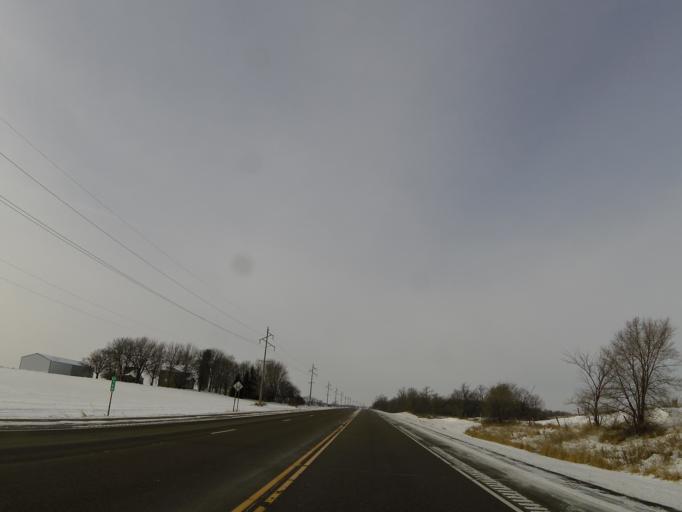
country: US
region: Minnesota
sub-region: Carver County
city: Mayer
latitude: 44.9056
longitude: -93.8488
